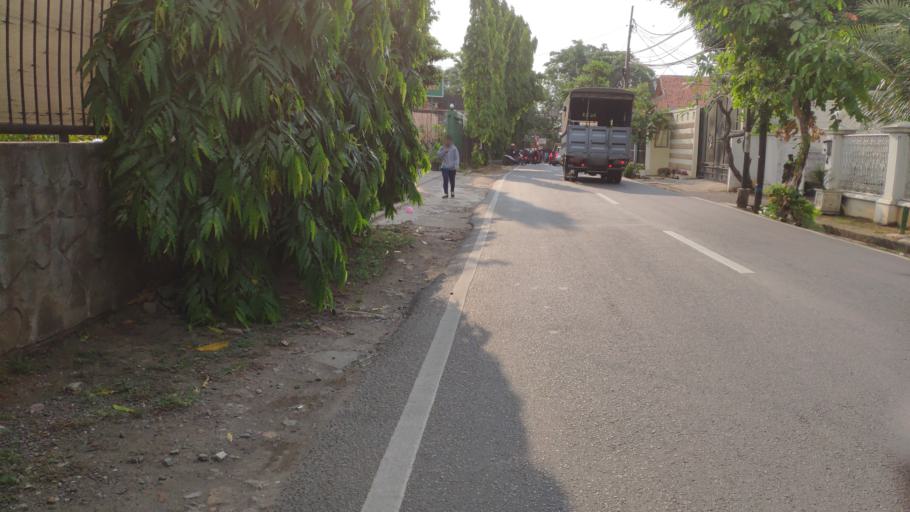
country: ID
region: West Java
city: Pamulang
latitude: -6.3158
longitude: 106.8125
